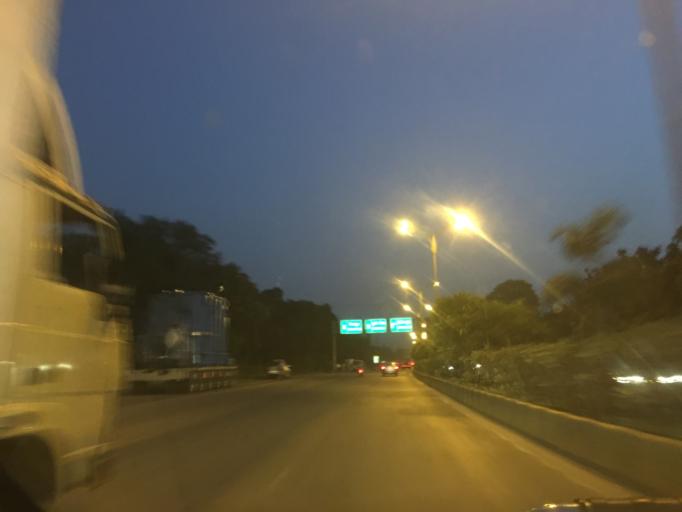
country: IN
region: Maharashtra
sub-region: Thane
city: Airoli
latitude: 19.1524
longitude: 73.0007
